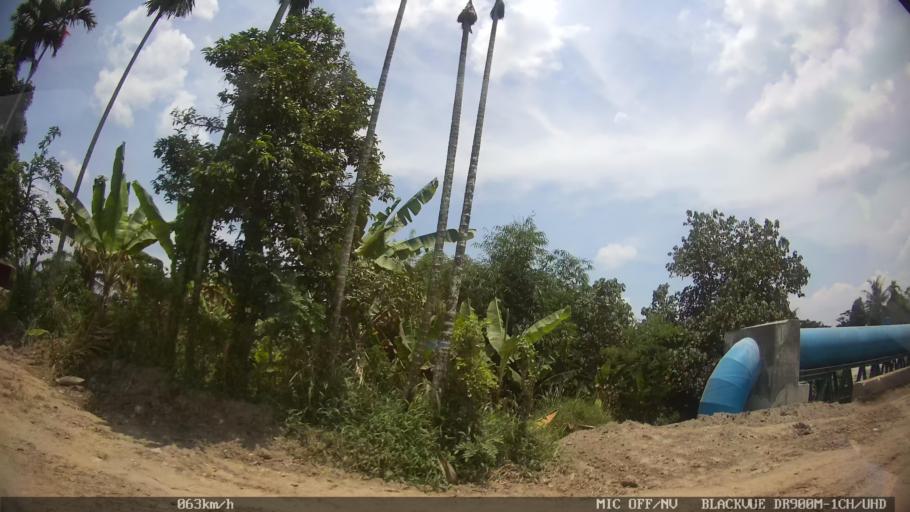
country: ID
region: North Sumatra
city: Binjai
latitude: 3.5899
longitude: 98.5479
